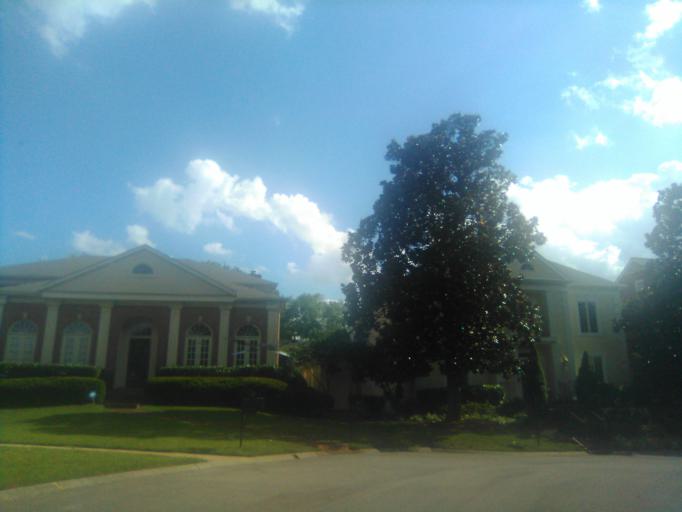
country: US
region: Tennessee
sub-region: Davidson County
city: Belle Meade
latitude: 36.1060
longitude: -86.8279
